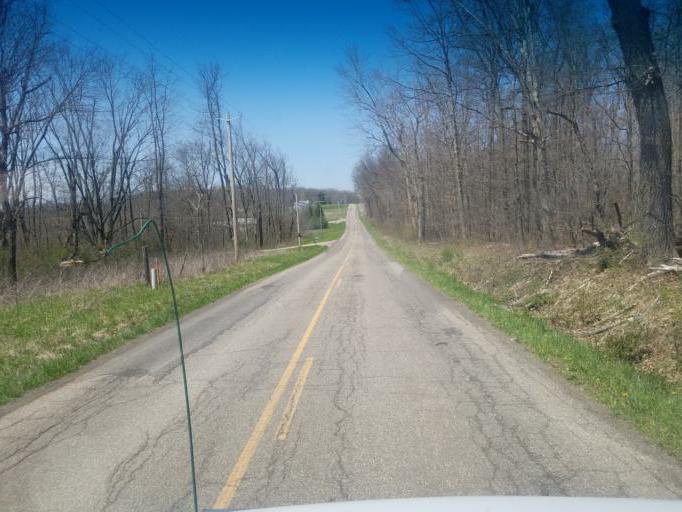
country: US
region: Ohio
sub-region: Knox County
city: Oak Hill
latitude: 40.3495
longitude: -82.2745
